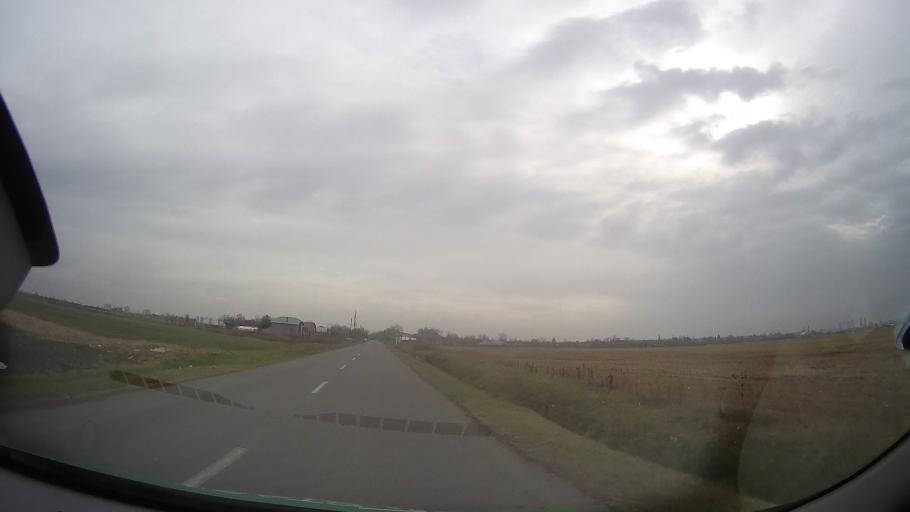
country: RO
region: Prahova
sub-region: Comuna Dumbrava
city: Dumbrava
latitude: 44.8801
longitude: 26.1812
